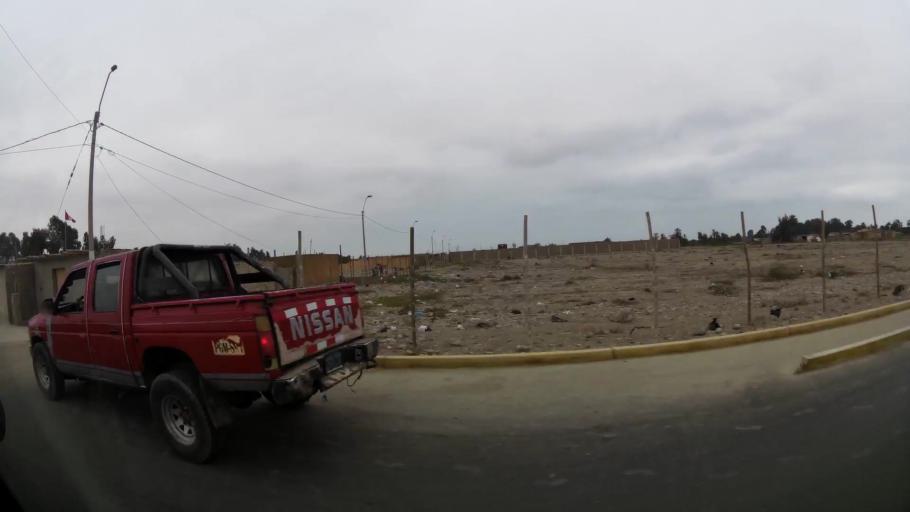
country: PE
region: Ica
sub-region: Provincia de Pisco
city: Pisco
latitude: -13.7284
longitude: -76.2020
